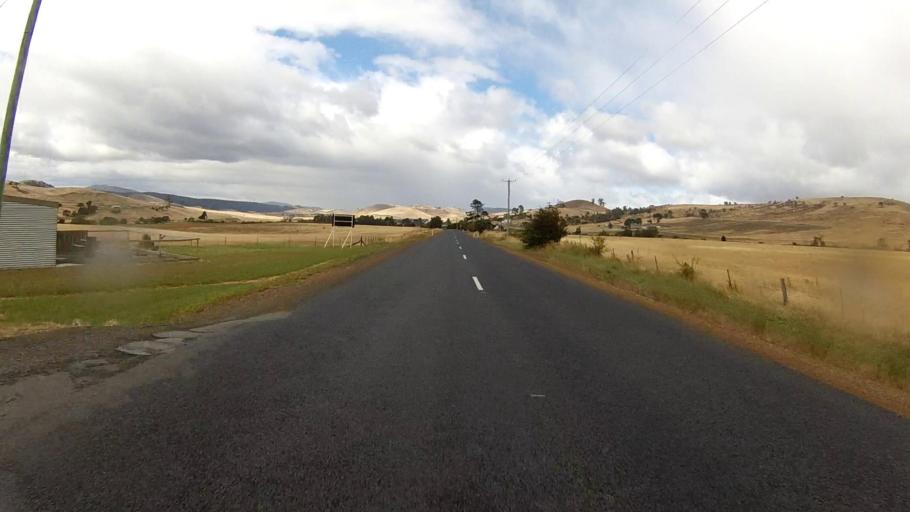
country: AU
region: Tasmania
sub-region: Brighton
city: Bridgewater
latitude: -42.5259
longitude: 147.3585
